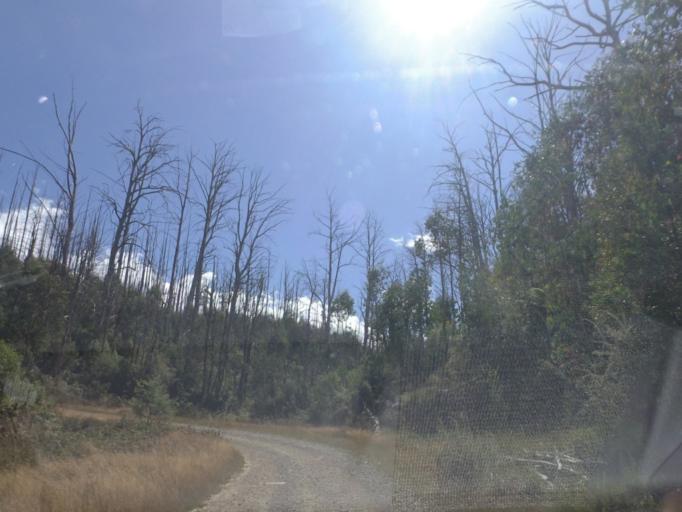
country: AU
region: Victoria
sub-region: Murrindindi
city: Alexandra
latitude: -37.4501
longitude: 145.8072
